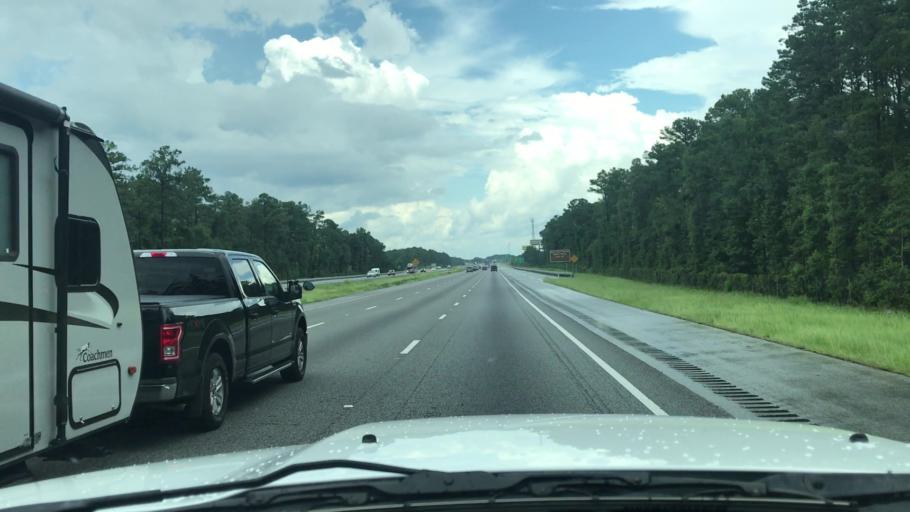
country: US
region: Georgia
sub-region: Liberty County
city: Midway
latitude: 31.6396
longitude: -81.4018
